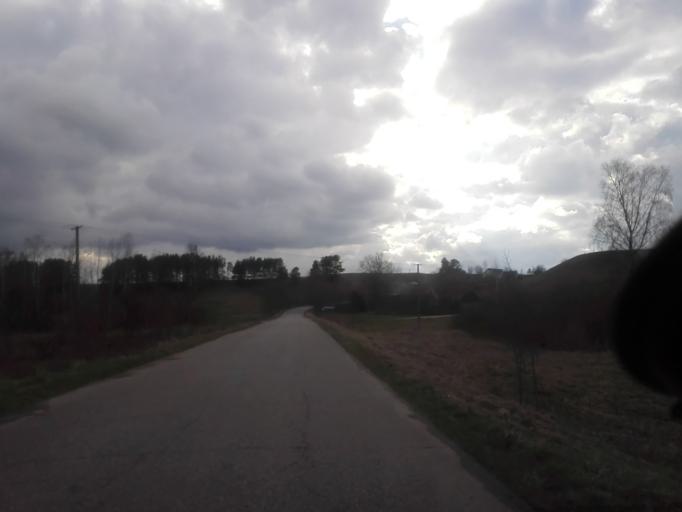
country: PL
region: Podlasie
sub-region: Suwalki
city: Suwalki
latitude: 54.2188
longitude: 22.8120
